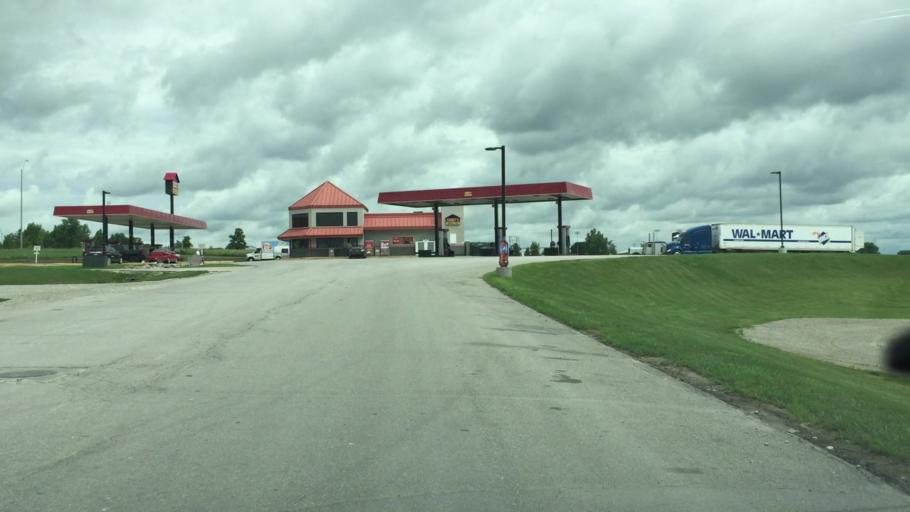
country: US
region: Iowa
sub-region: Jasper County
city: Monroe
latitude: 41.5089
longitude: -93.0998
